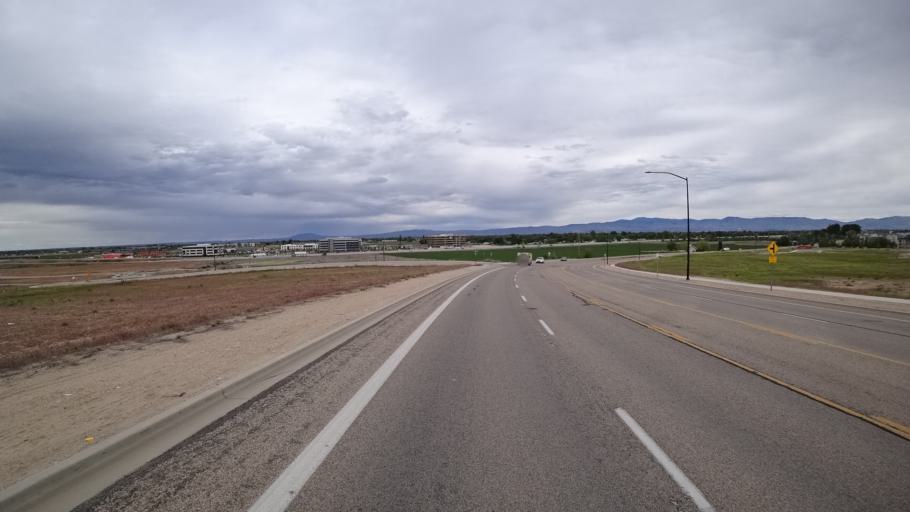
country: US
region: Idaho
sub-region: Ada County
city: Meridian
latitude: 43.5888
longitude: -116.4278
